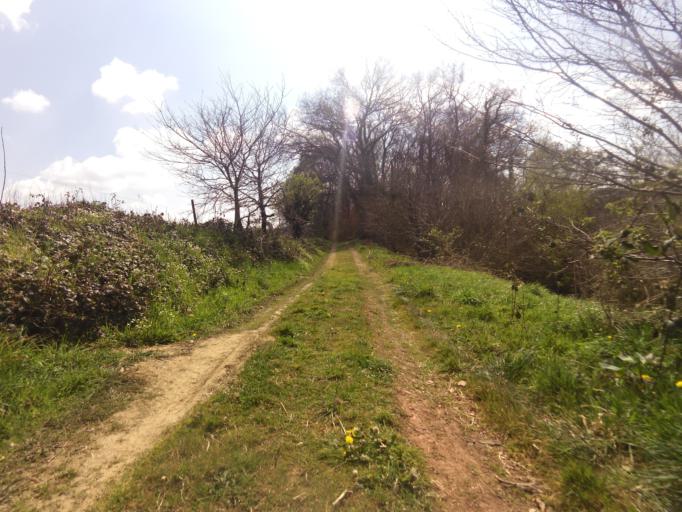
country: FR
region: Brittany
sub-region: Departement du Morbihan
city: Molac
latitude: 47.7158
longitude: -2.4055
